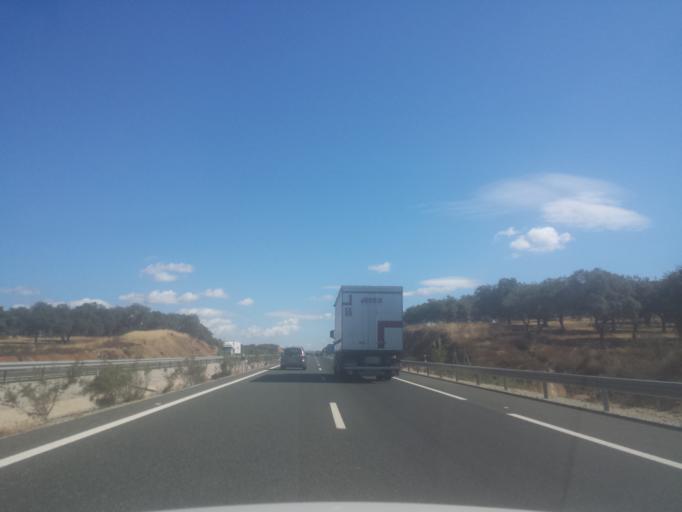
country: ES
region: Andalusia
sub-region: Provincia de Huelva
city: Santa Olalla del Cala
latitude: 37.8935
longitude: -6.2163
